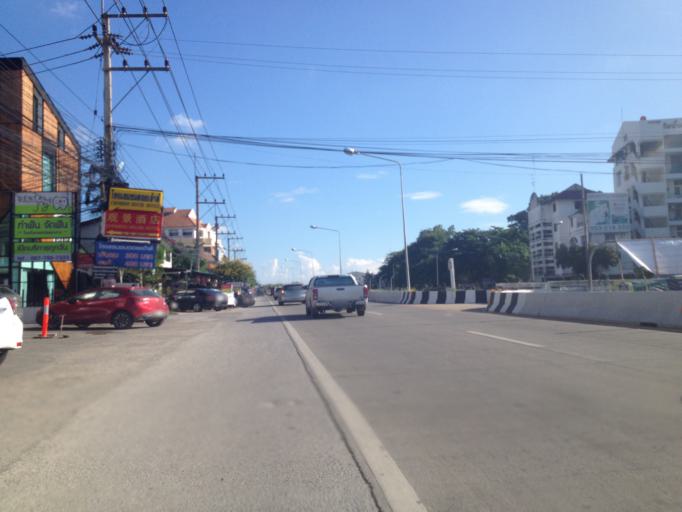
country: TH
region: Chiang Mai
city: Chiang Mai
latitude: 18.8006
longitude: 98.9605
